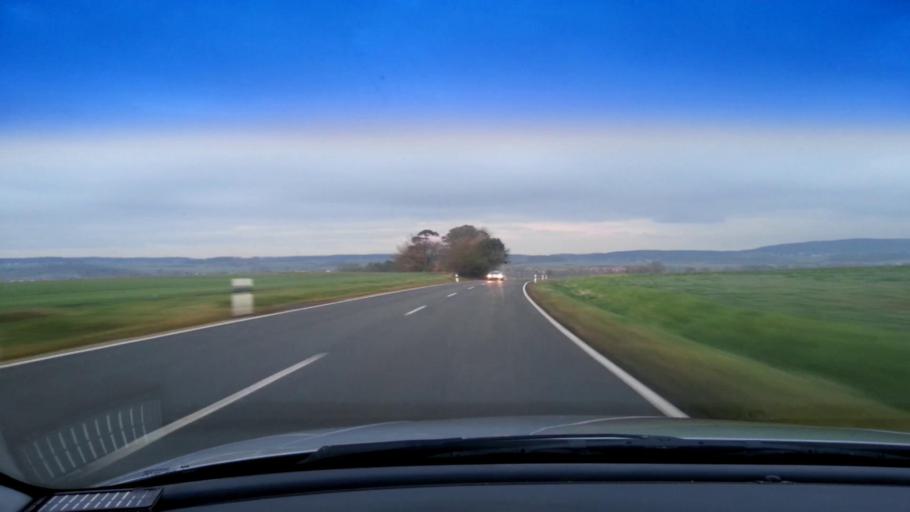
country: DE
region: Bavaria
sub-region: Upper Franconia
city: Frensdorf
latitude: 49.8126
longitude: 10.8390
